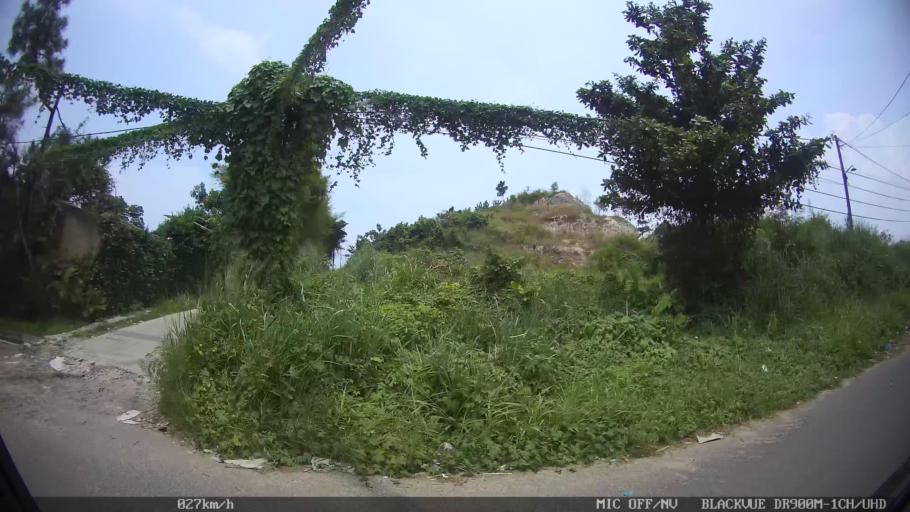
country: ID
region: Lampung
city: Bandarlampung
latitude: -5.4144
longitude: 105.2717
